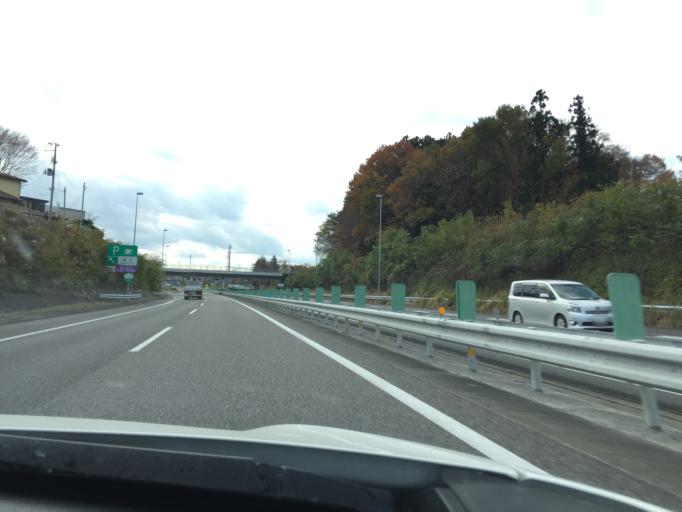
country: JP
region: Fukushima
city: Sukagawa
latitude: 37.2582
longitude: 140.3383
